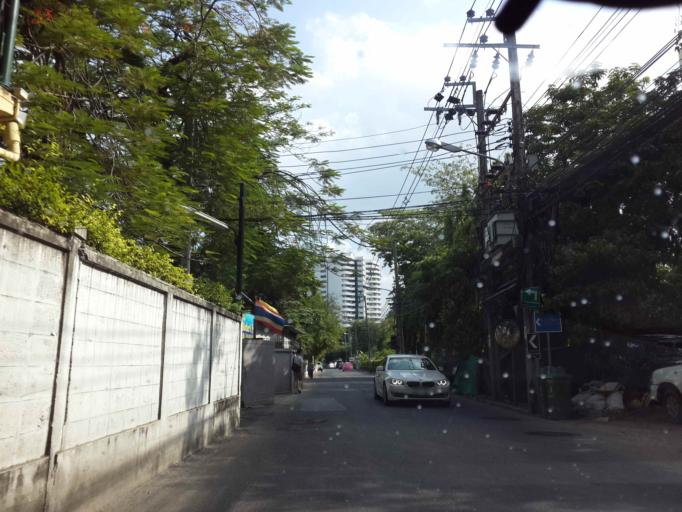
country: TH
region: Bangkok
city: Yan Nawa
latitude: 13.7143
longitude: 100.5456
